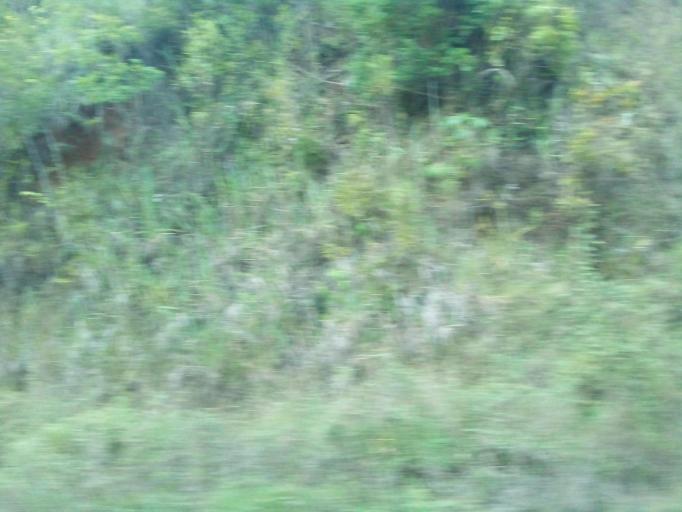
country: BR
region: Minas Gerais
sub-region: Caete
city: Caete
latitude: -19.9128
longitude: -43.7068
